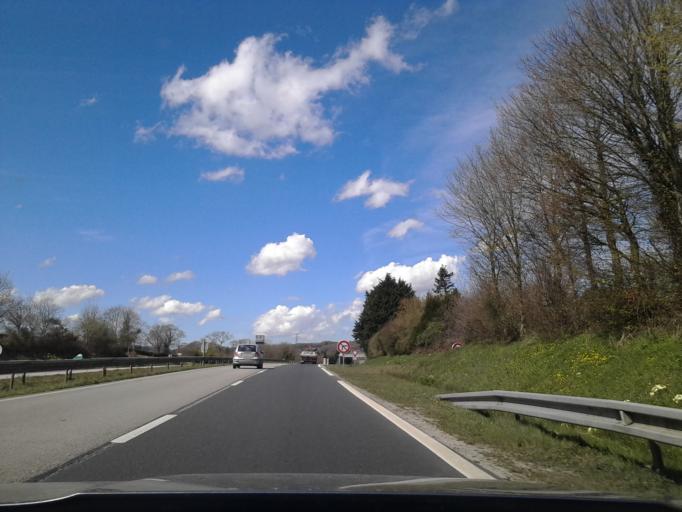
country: FR
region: Lower Normandy
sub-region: Departement de la Manche
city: Brix
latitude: 49.5338
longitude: -1.5318
